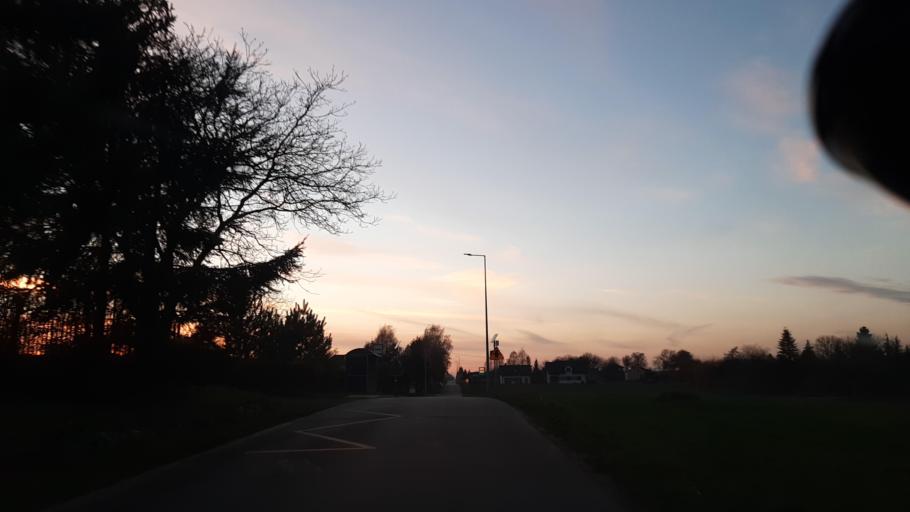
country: PL
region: Lublin Voivodeship
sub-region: Powiat lubelski
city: Jastkow
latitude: 51.3235
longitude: 22.4573
